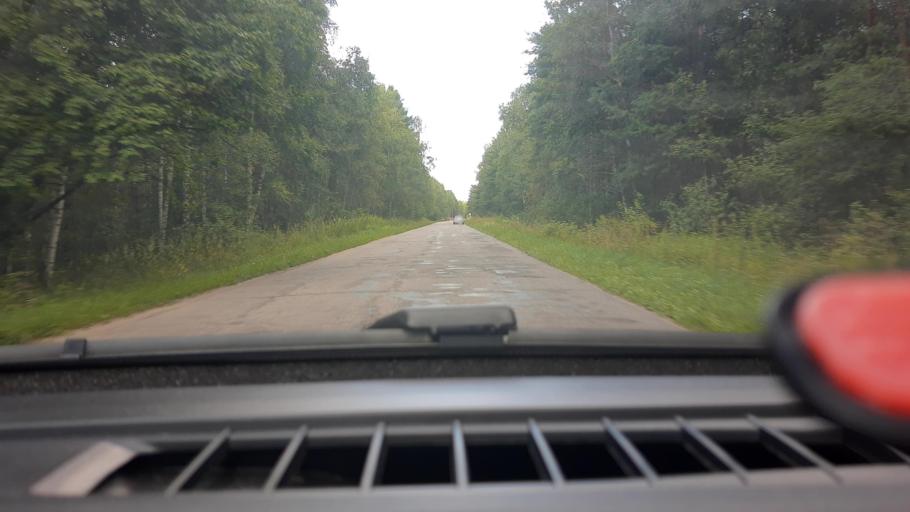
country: RU
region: Nizjnij Novgorod
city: Babino
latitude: 56.3281
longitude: 43.6342
